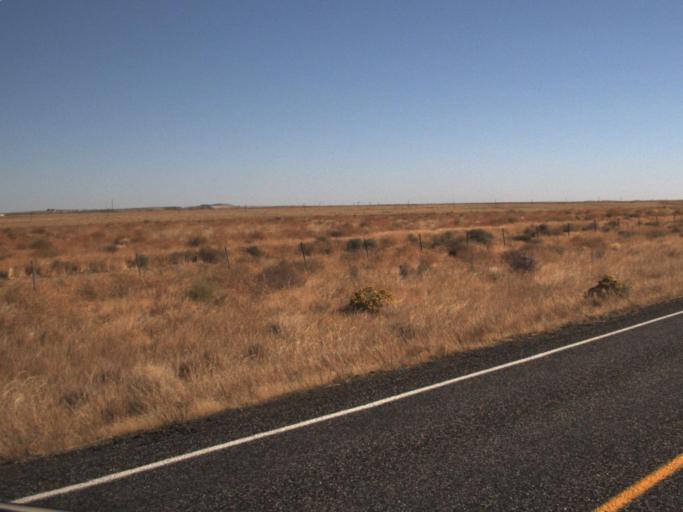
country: US
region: Washington
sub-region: Benton County
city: Benton City
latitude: 46.5092
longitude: -119.6520
